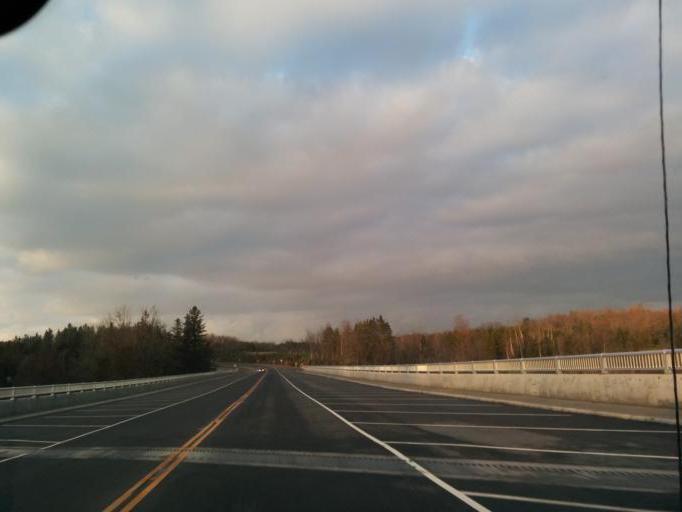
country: CA
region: Ontario
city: Brampton
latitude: 43.8830
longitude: -79.7725
